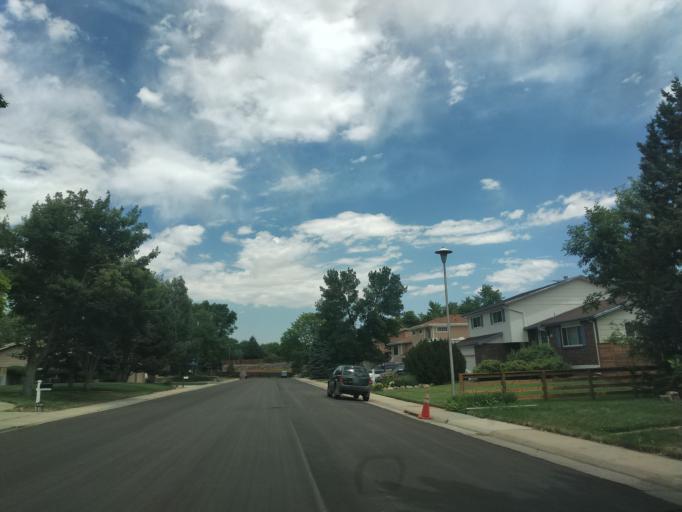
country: US
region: Colorado
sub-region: Jefferson County
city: Lakewood
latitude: 39.6727
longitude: -105.0978
